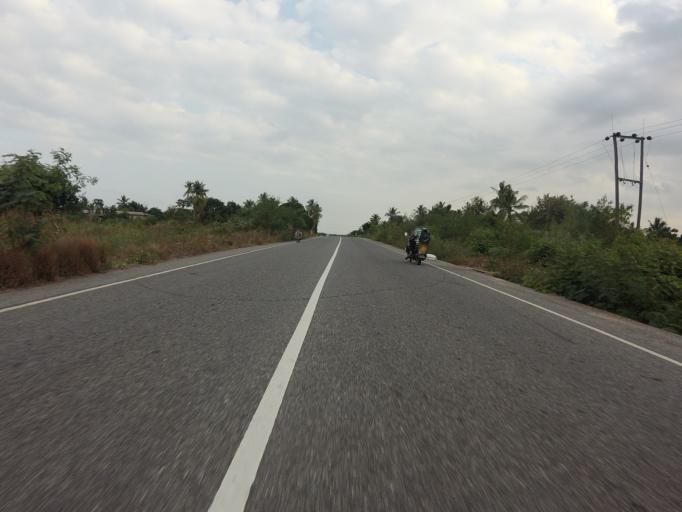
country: GH
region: Volta
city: Ho
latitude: 6.2503
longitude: 0.5507
